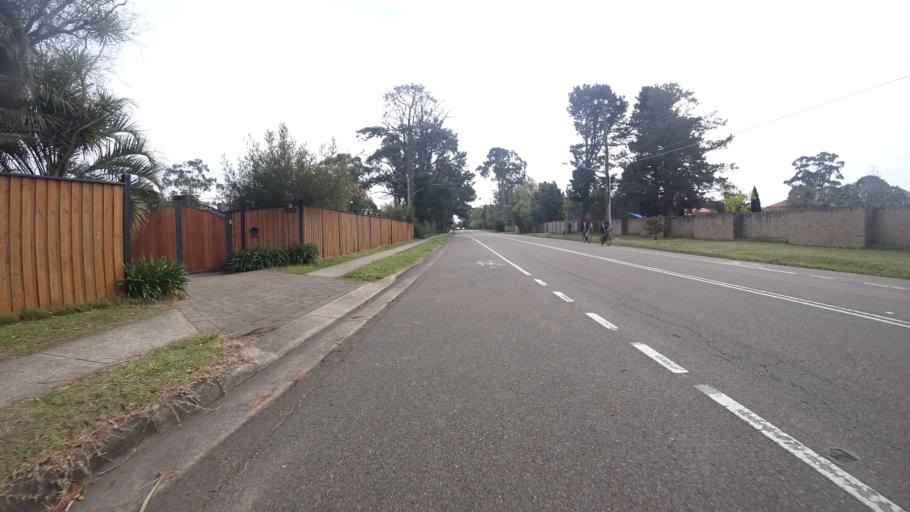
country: AU
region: New South Wales
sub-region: City of Sydney
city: North Turramurra
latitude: -33.6950
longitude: 151.1514
